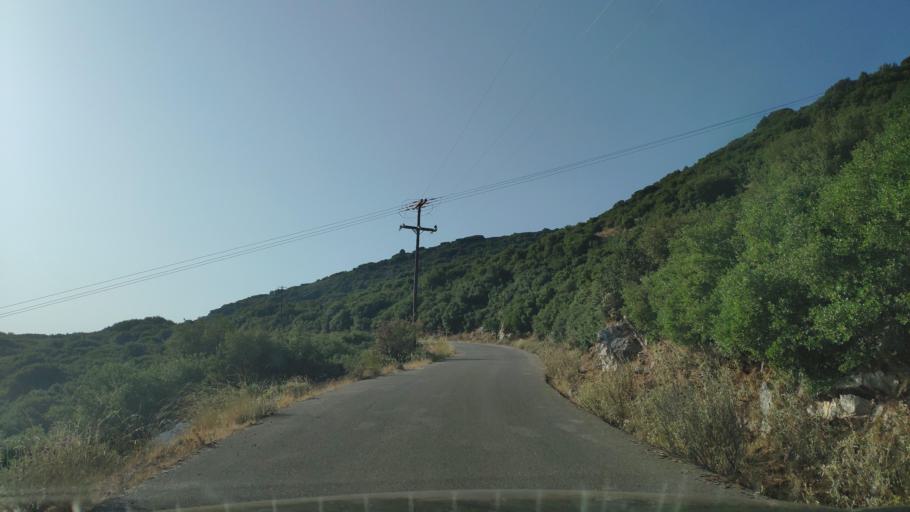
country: GR
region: West Greece
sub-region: Nomos Aitolias kai Akarnanias
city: Monastirakion
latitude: 38.8432
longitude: 20.9762
